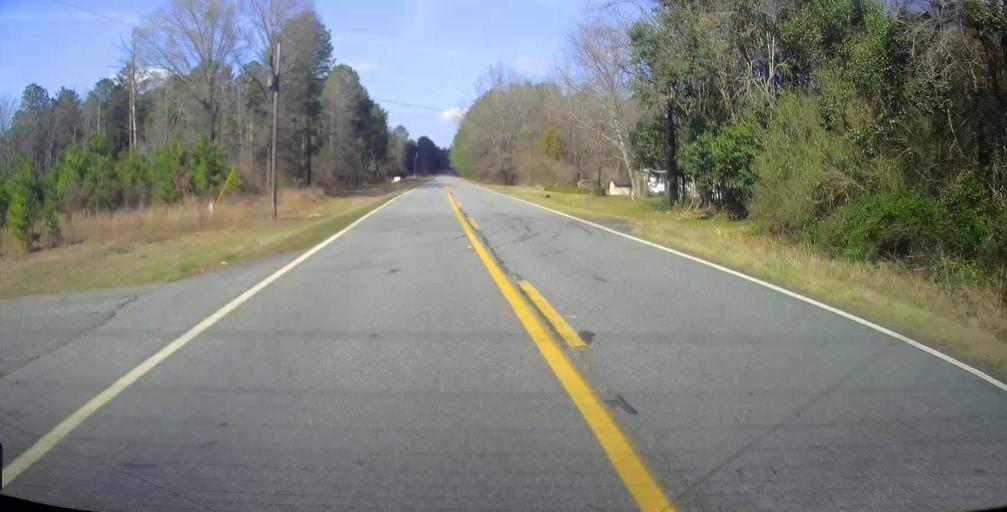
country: US
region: Georgia
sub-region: Twiggs County
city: Jeffersonville
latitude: 32.7573
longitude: -83.3434
